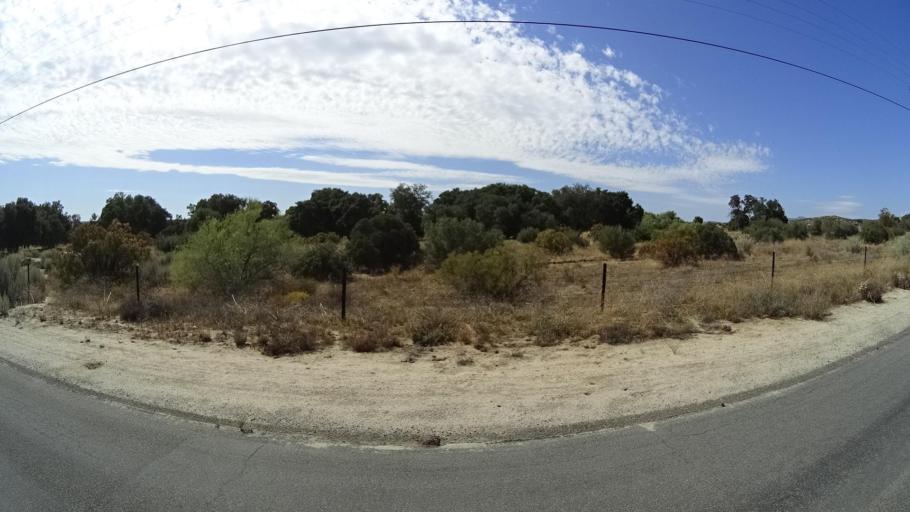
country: MX
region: Baja California
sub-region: Tecate
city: Cereso del Hongo
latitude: 32.6919
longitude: -116.2598
